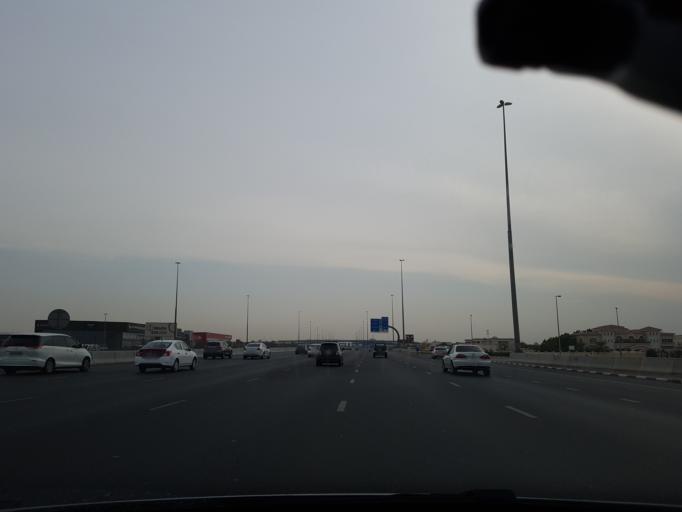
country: AE
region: Ash Shariqah
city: Sharjah
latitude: 25.3443
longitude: 55.4722
